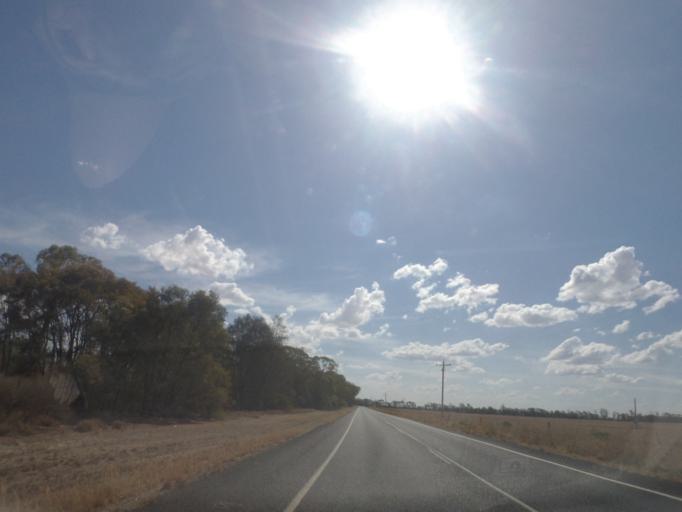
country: AU
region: Queensland
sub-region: Southern Downs
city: Stanthorpe
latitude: -28.4034
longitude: 151.1860
